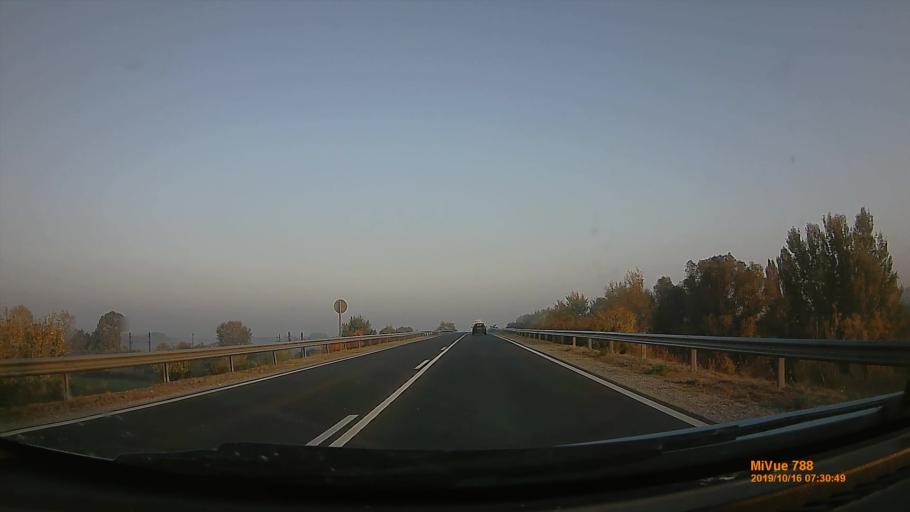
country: HU
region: Heves
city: Fuzesabony
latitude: 47.7467
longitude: 20.3994
